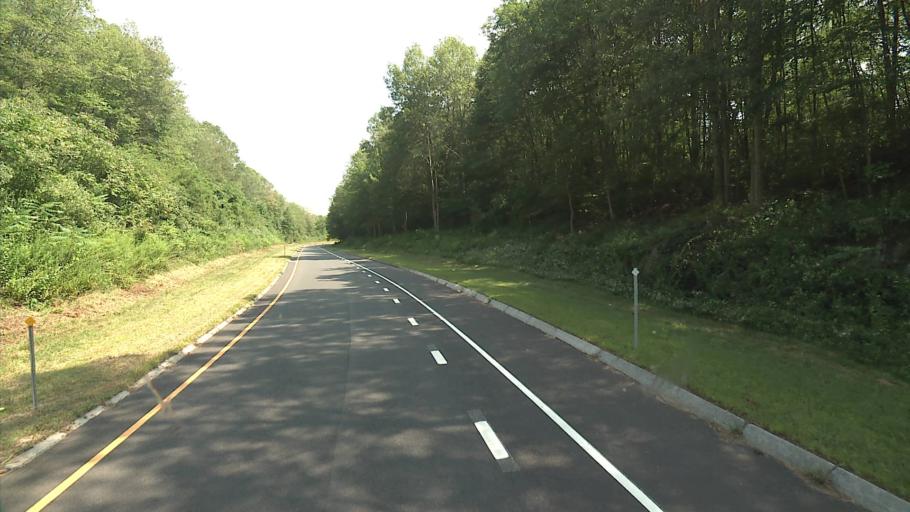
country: US
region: Connecticut
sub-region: Middlesex County
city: Chester Center
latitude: 41.4151
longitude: -72.4921
